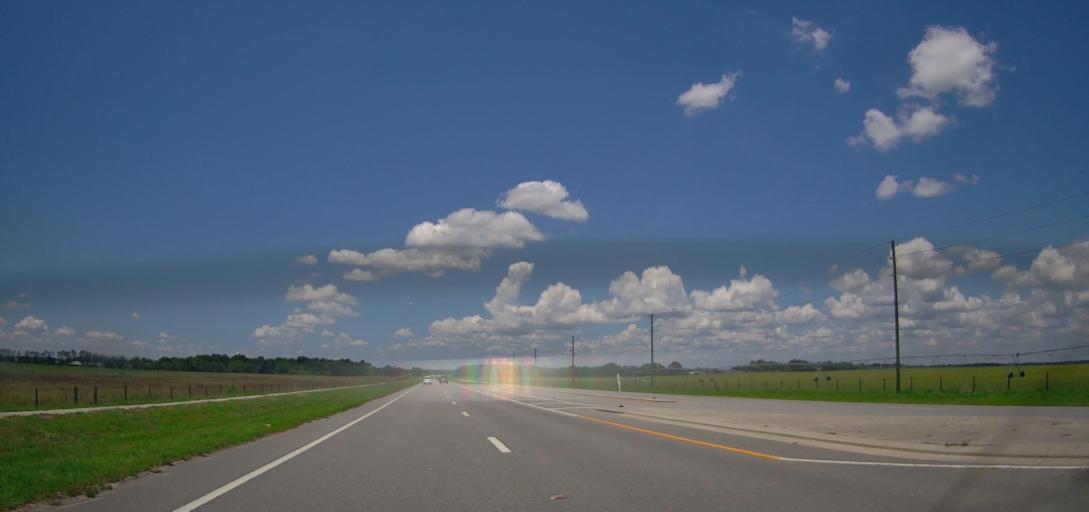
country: US
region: Florida
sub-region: Marion County
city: Silver Springs Shores
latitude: 29.0732
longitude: -82.0288
